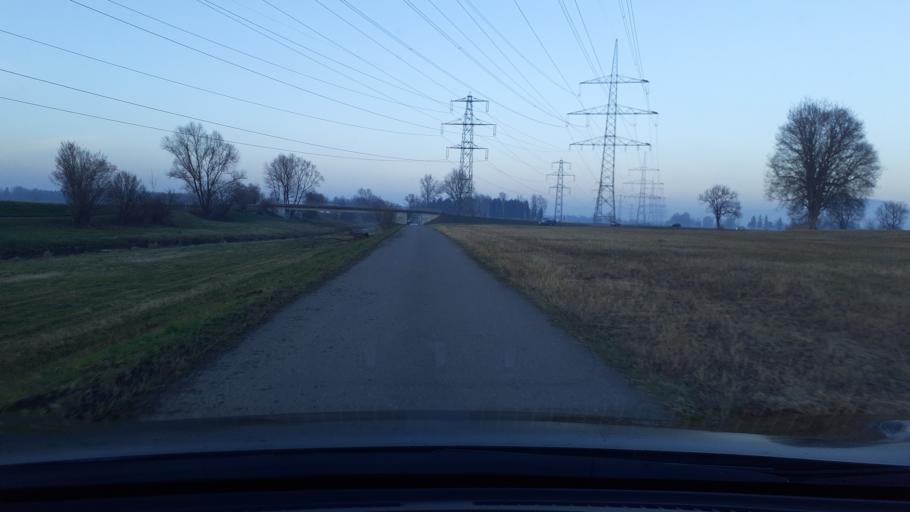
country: AT
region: Vorarlberg
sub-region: Politischer Bezirk Dornbirn
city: Hohenems
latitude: 47.3971
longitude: 9.6856
